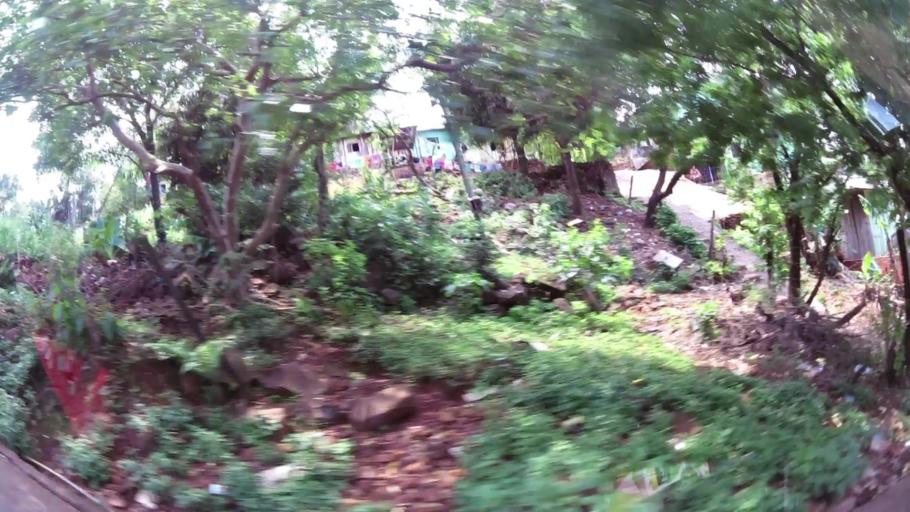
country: PY
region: Alto Parana
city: Ciudad del Este
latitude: -25.5035
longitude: -54.6180
